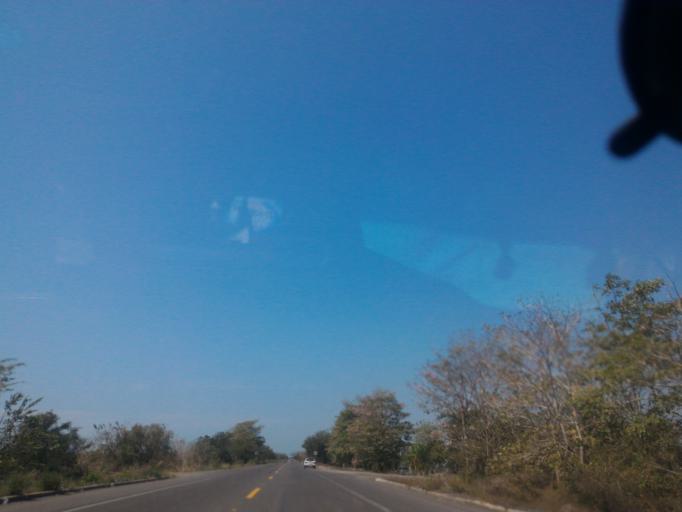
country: MX
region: Michoacan
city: Coahuayana Viejo
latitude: 18.7778
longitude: -103.7565
